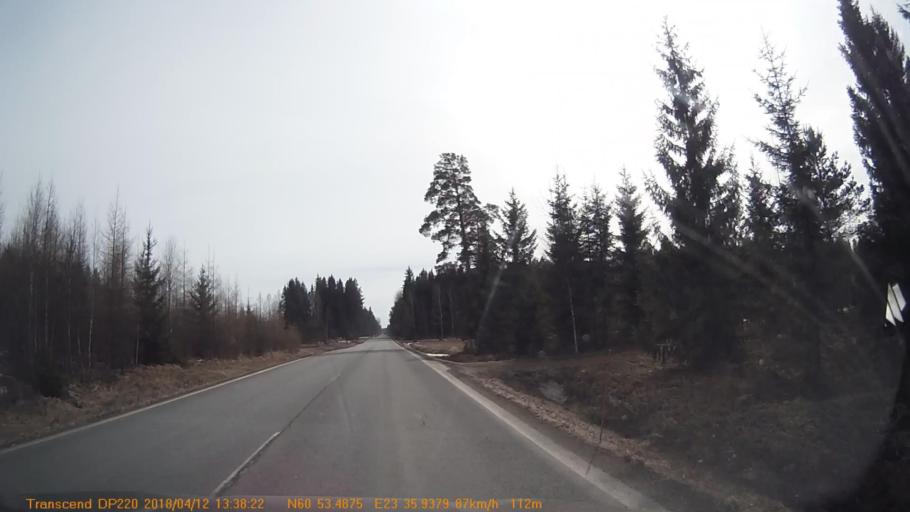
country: FI
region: Haeme
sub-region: Forssa
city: Forssa
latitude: 60.8912
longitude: 23.5991
